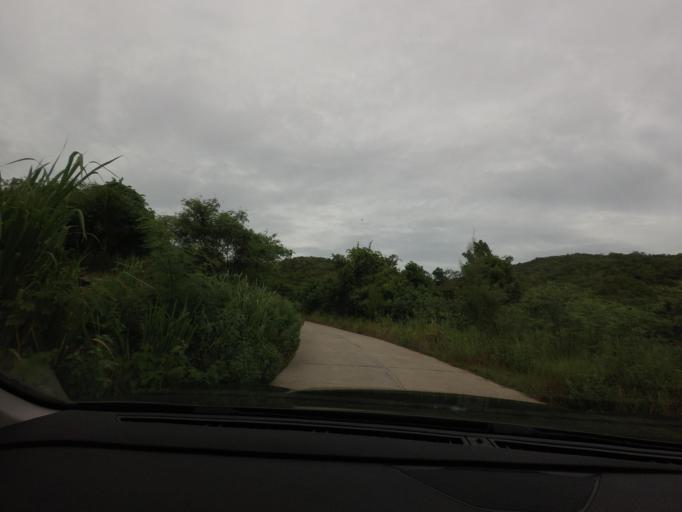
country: TH
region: Prachuap Khiri Khan
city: Hua Hin
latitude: 12.4845
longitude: 99.9422
